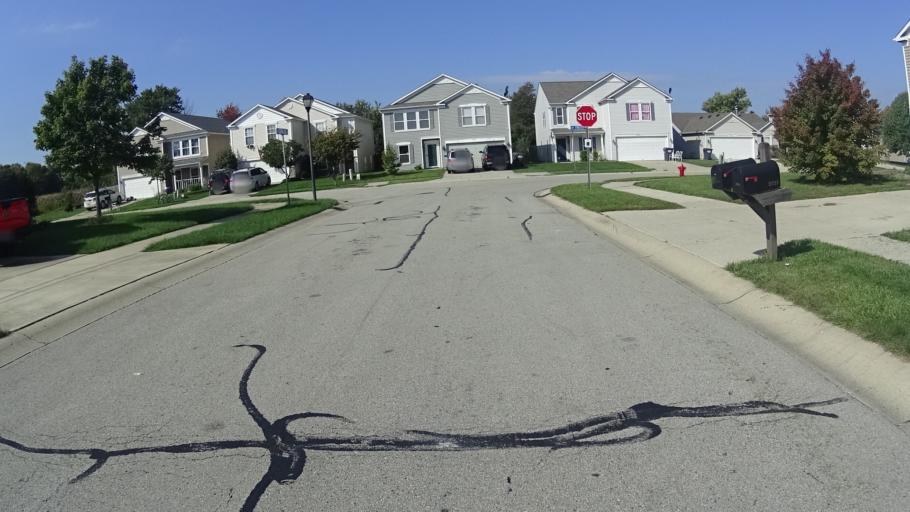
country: US
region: Indiana
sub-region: Hancock County
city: Fortville
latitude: 39.9808
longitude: -85.8565
